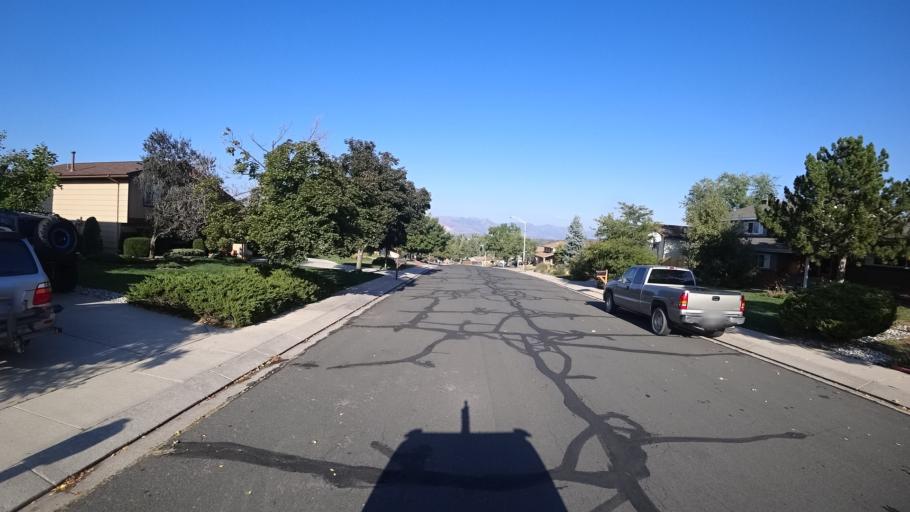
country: US
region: Colorado
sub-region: El Paso County
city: Cimarron Hills
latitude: 38.8874
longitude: -104.7324
